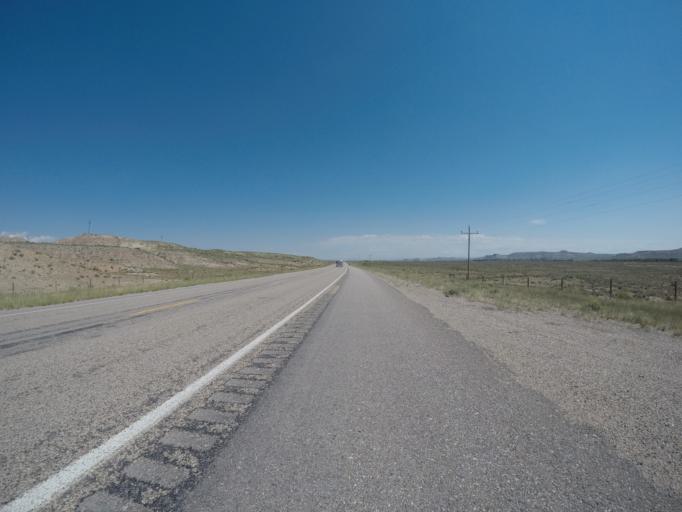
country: US
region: Wyoming
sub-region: Sublette County
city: Marbleton
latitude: 42.3945
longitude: -110.1263
